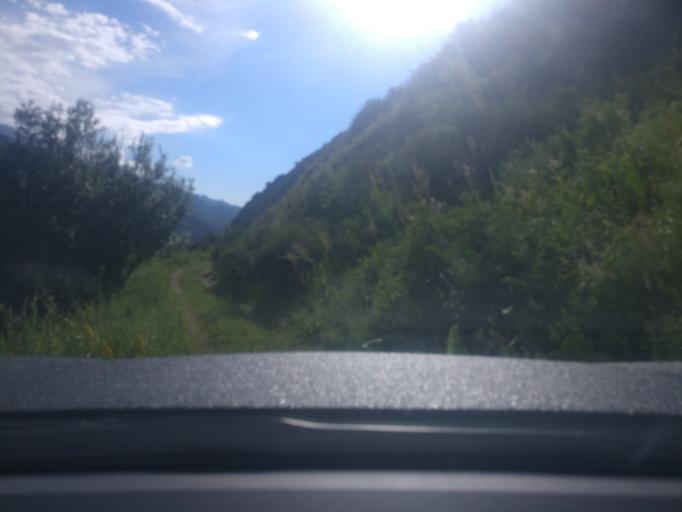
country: KZ
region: Almaty Qalasy
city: Almaty
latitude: 43.1075
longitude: 76.9520
